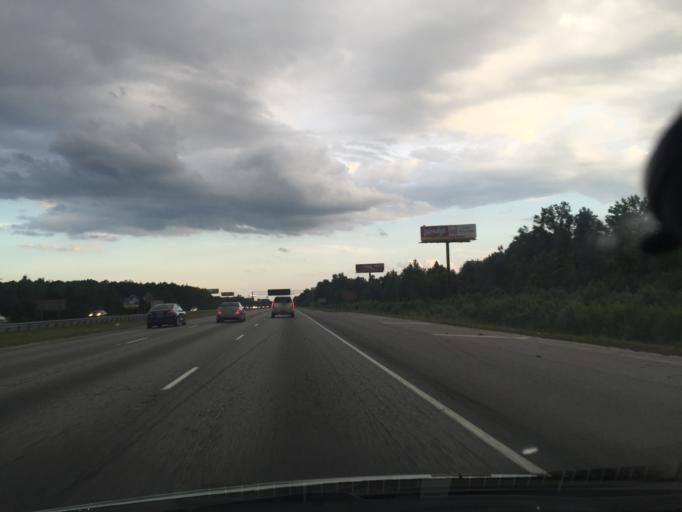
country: US
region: Georgia
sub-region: Chatham County
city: Pooler
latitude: 32.1298
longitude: -81.2398
